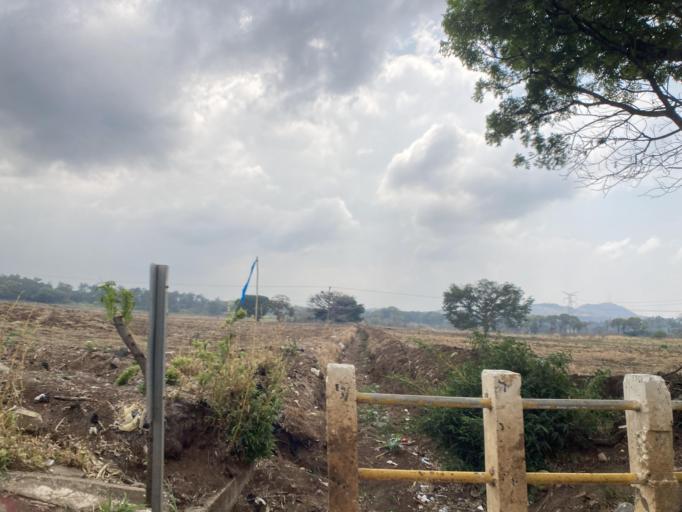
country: GT
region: Guatemala
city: Fraijanes
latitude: 14.3928
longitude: -90.4835
